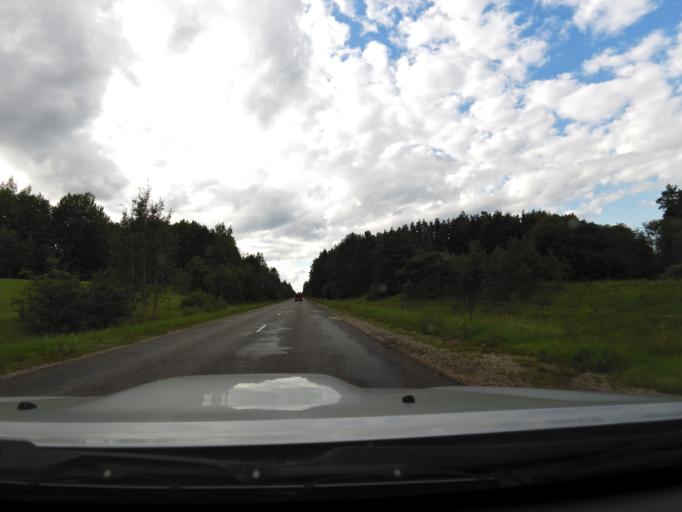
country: LV
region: Akniste
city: Akniste
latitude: 56.0048
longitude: 25.9471
